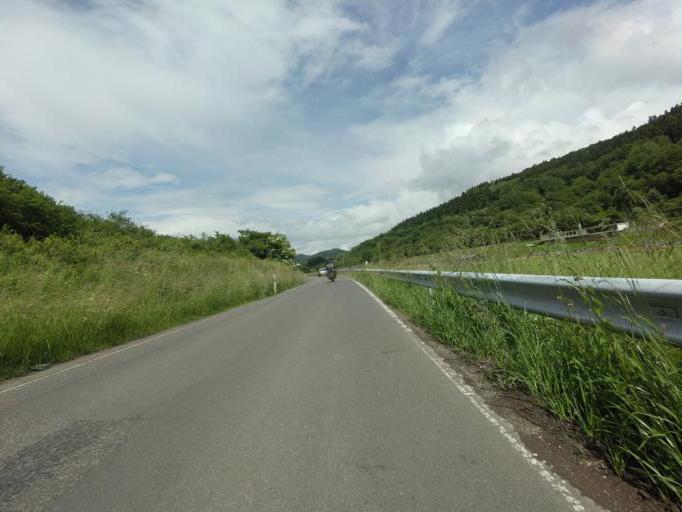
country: DE
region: Rheinland-Pfalz
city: Wimbach
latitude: 50.3742
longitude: 6.9224
